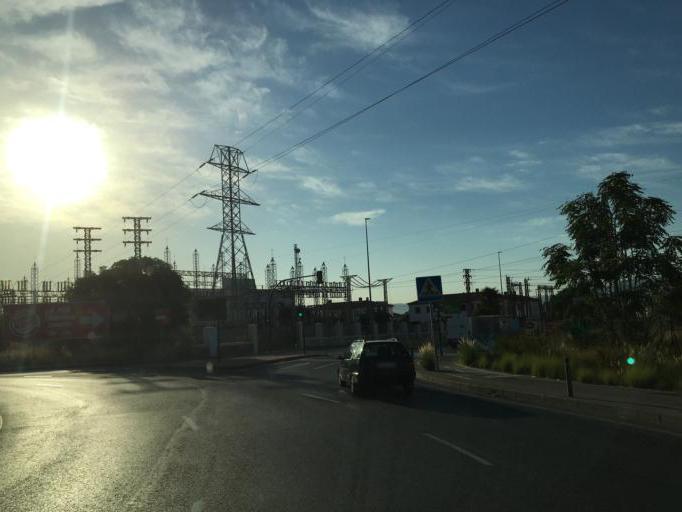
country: ES
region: Murcia
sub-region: Murcia
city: Murcia
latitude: 38.0169
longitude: -1.1592
